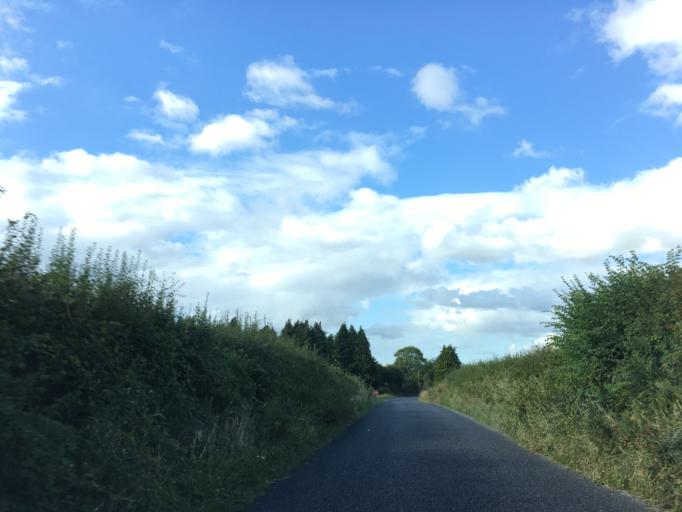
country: IE
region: Munster
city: Cahir
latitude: 52.2697
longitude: -7.9566
